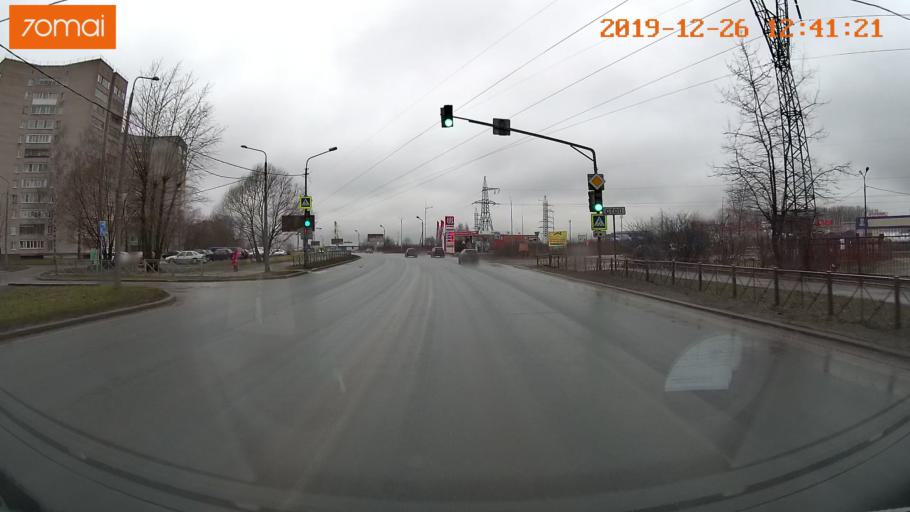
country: RU
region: Vologda
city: Tonshalovo
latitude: 59.1488
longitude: 37.9629
